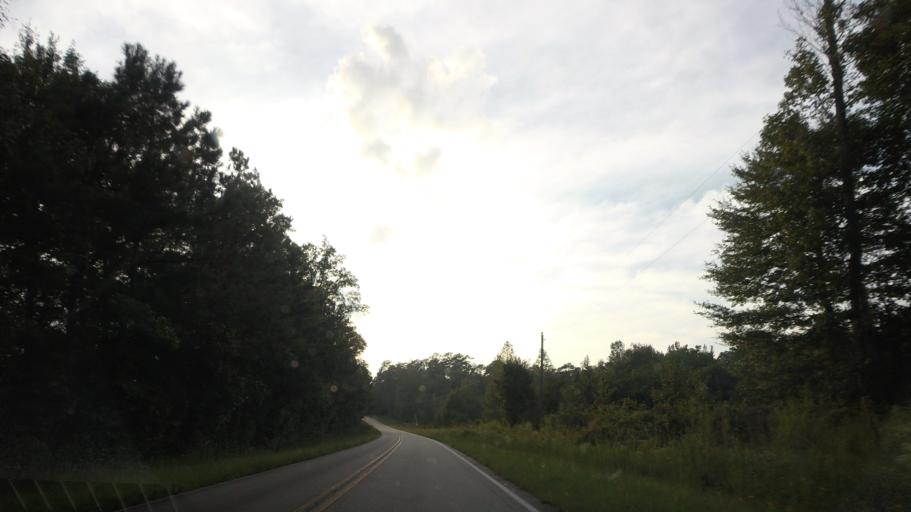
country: US
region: Georgia
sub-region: Bibb County
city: Macon
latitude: 32.8734
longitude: -83.4960
